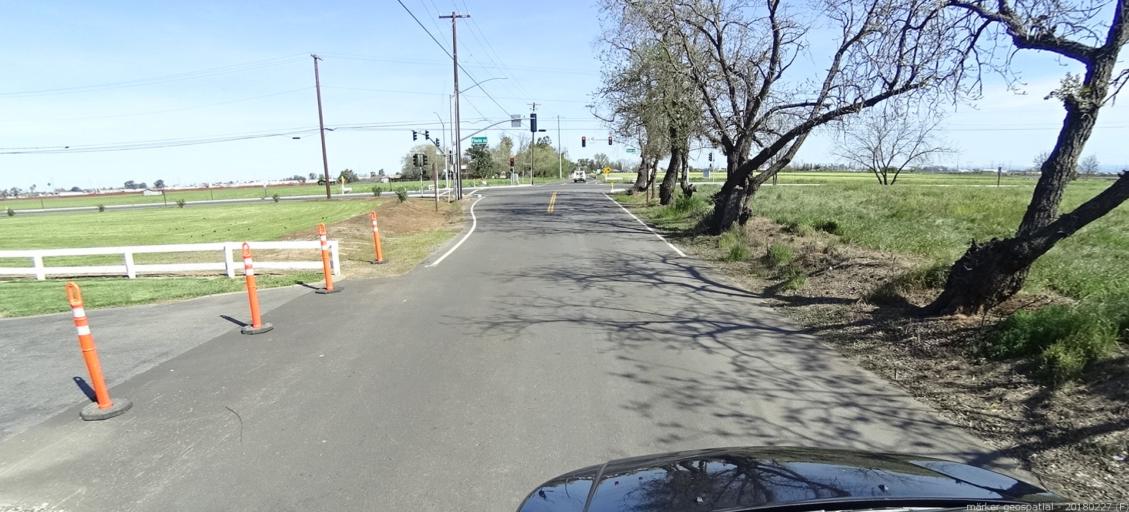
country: US
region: California
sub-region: Sacramento County
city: Vineyard
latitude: 38.4957
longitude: -121.3627
